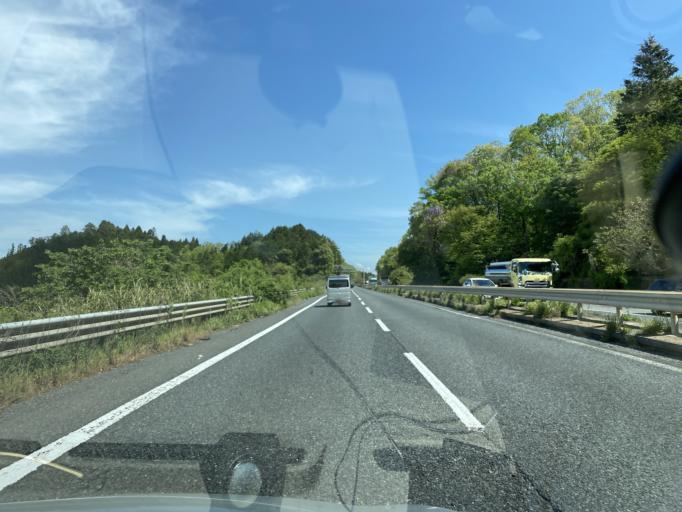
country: JP
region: Mie
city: Nabari
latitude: 34.6652
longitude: 136.0329
